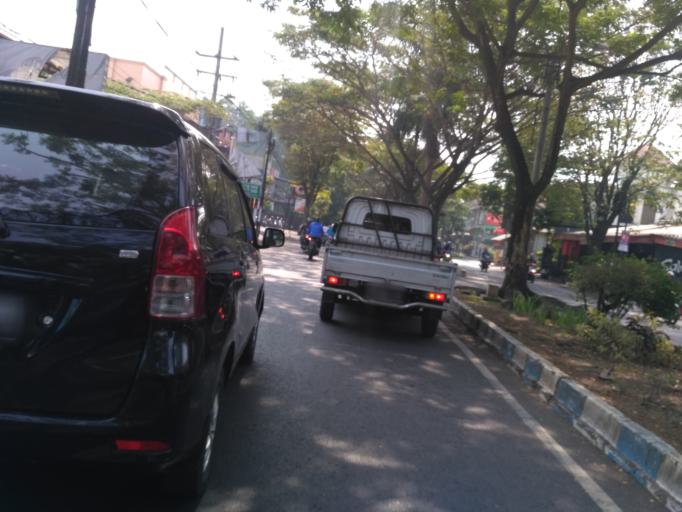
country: ID
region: East Java
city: Malang
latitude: -7.9757
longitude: 112.6615
